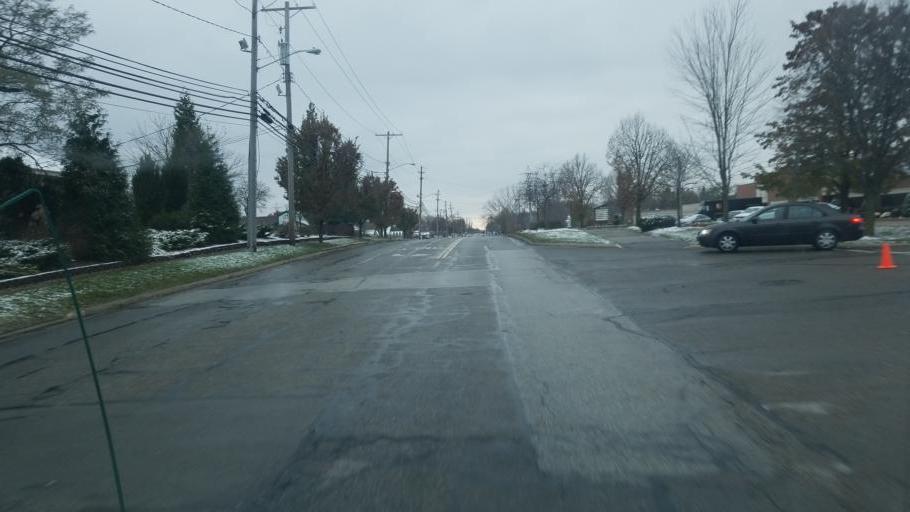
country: US
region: Ohio
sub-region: Cuyahoga County
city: Oakwood
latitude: 41.3599
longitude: -81.5014
